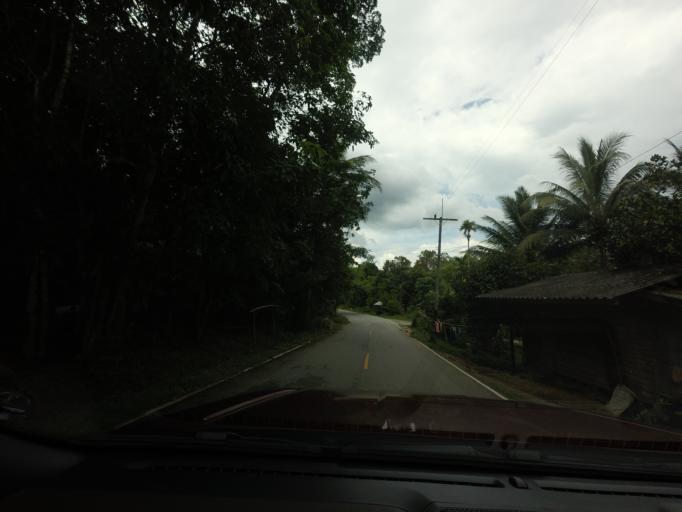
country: TH
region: Narathiwat
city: Sukhirin
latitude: 5.9907
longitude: 101.7048
